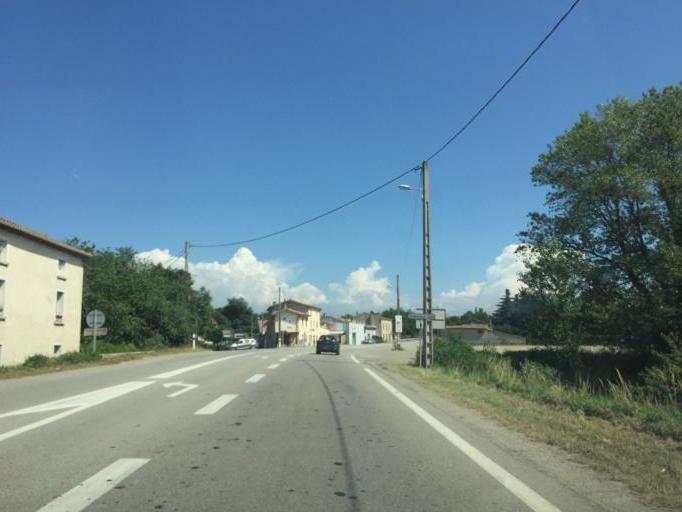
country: FR
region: Rhone-Alpes
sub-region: Departement de l'Ardeche
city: Tournon-sur-Rhone
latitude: 45.0586
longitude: 4.8640
